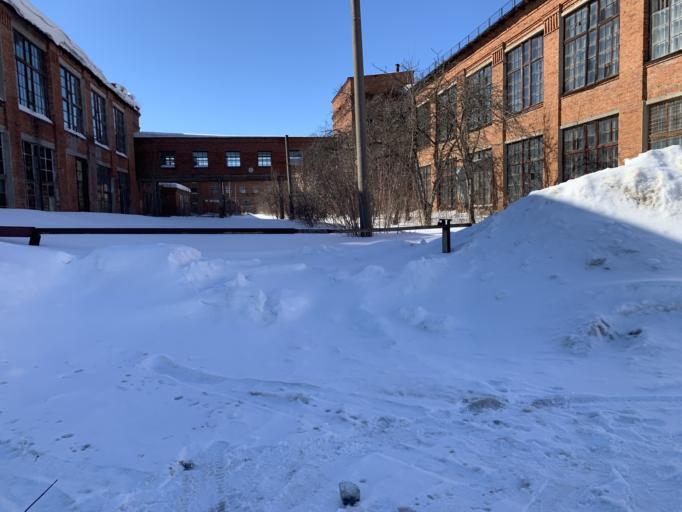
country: RU
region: Chuvashia
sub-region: Cheboksarskiy Rayon
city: Cheboksary
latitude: 56.1456
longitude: 47.2778
